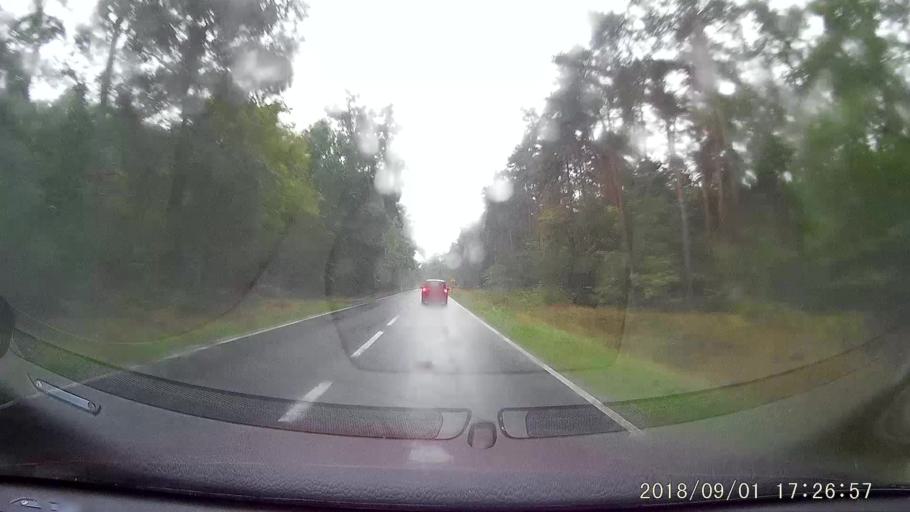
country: PL
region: Lubusz
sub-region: Powiat zaganski
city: Zagan
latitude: 51.6717
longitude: 15.3091
